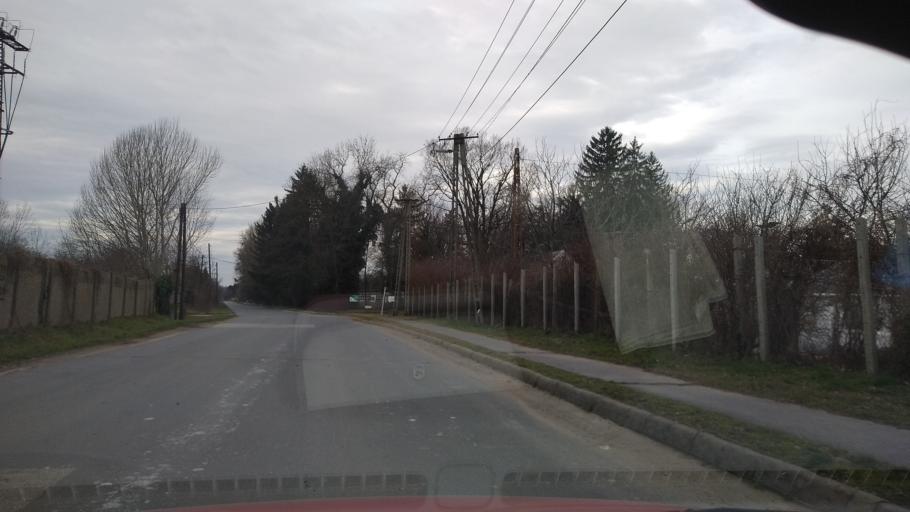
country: HU
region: Somogy
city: Barcs
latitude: 45.9533
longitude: 17.4418
